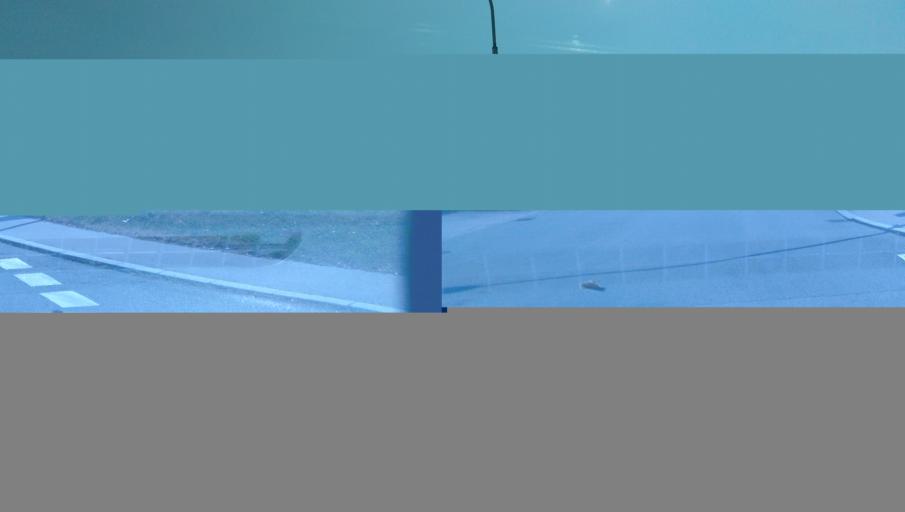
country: AT
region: Tyrol
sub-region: Politischer Bezirk Innsbruck Land
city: Ampass
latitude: 47.2680
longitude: 11.4324
